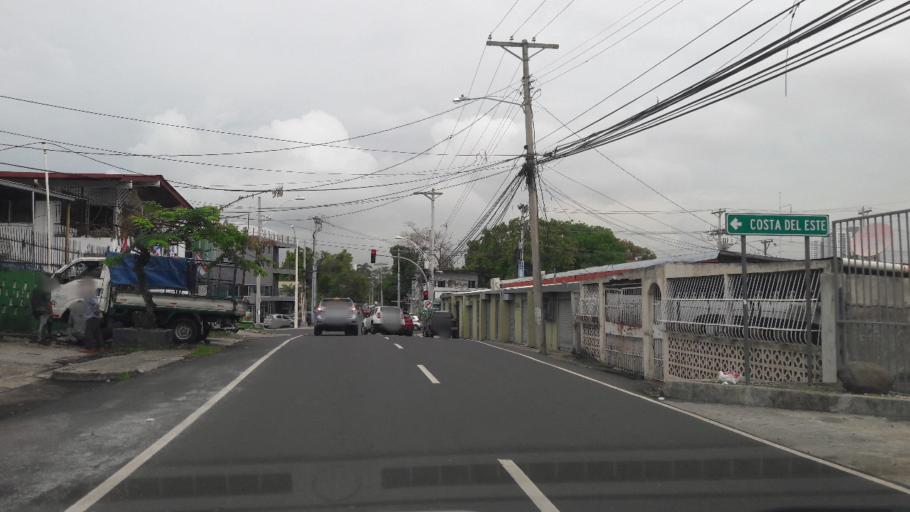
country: PA
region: Panama
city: San Miguelito
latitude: 9.0165
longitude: -79.4858
